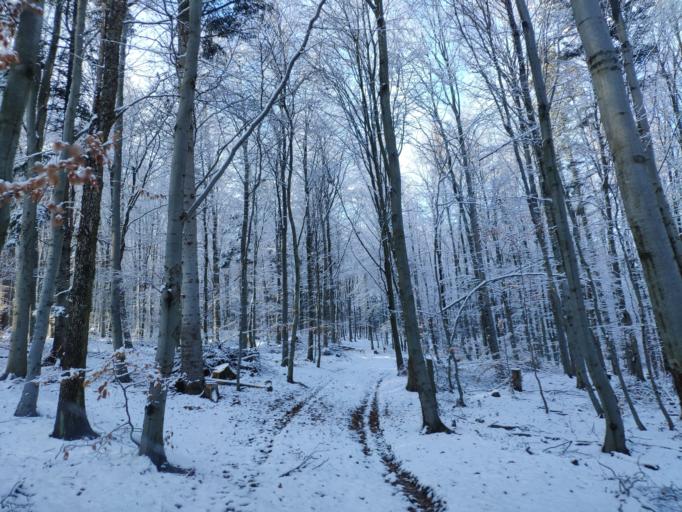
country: SK
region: Kosicky
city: Moldava nad Bodvou
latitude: 48.7442
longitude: 21.0873
